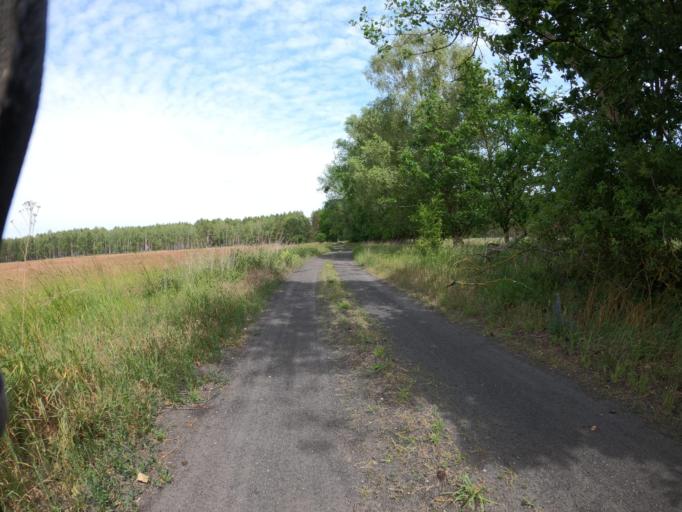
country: DE
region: Brandenburg
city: Zechin
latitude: 52.6796
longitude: 14.4883
